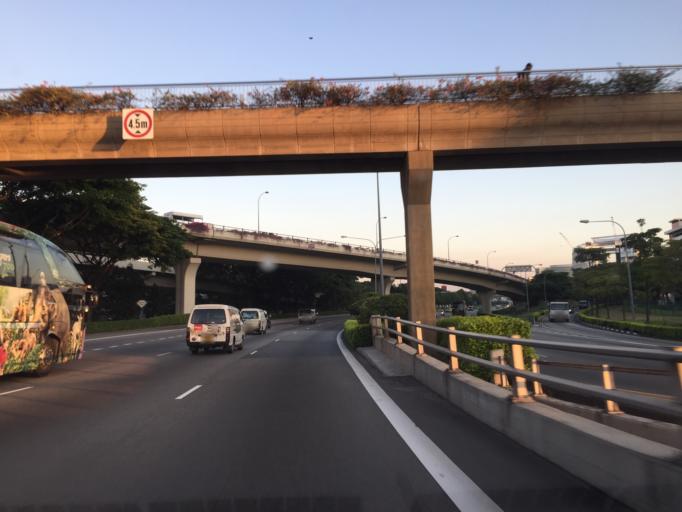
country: SG
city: Singapore
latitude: 1.3203
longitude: 103.8756
